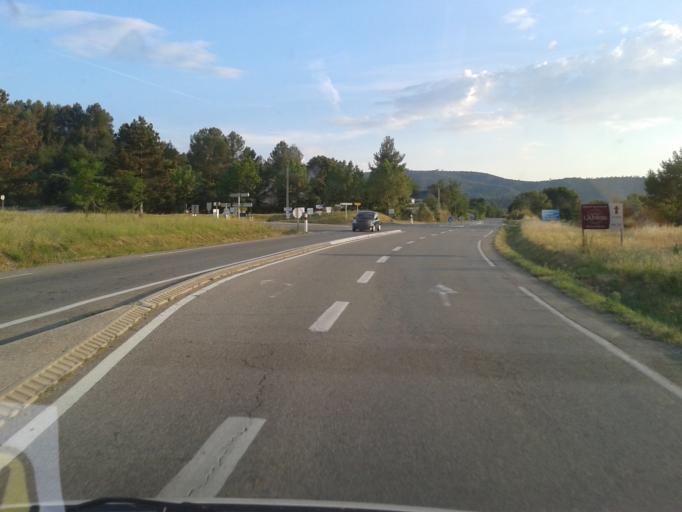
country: FR
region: Provence-Alpes-Cote d'Azur
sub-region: Departement du Vaucluse
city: Beaumont-de-Pertuis
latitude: 43.6976
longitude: 5.7328
